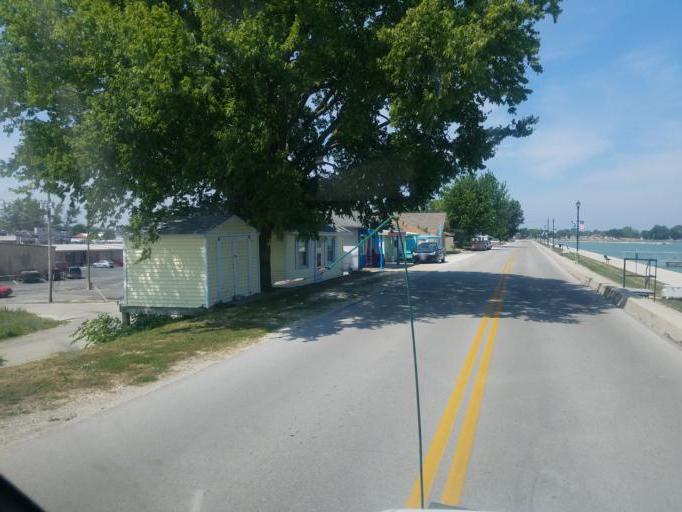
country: US
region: Ohio
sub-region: Mercer County
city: Celina
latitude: 40.5379
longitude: -84.5738
